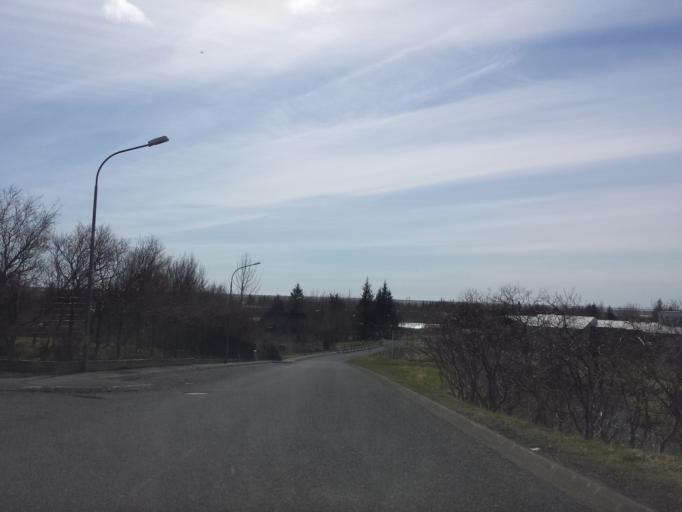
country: IS
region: South
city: Hveragerdi
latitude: 64.0020
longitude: -21.1809
